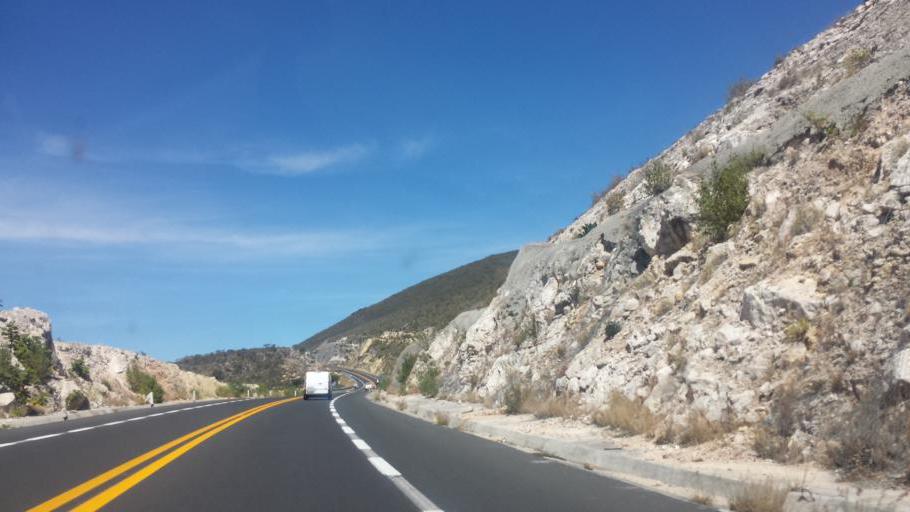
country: MX
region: Oaxaca
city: San Gabriel Casa Blanca
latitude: 17.9915
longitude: -97.3549
